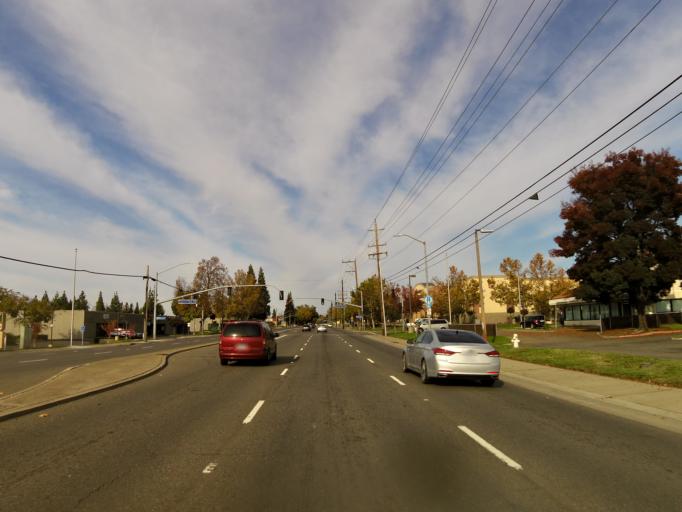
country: US
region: California
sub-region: Sacramento County
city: Rancho Cordova
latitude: 38.5931
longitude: -121.2655
